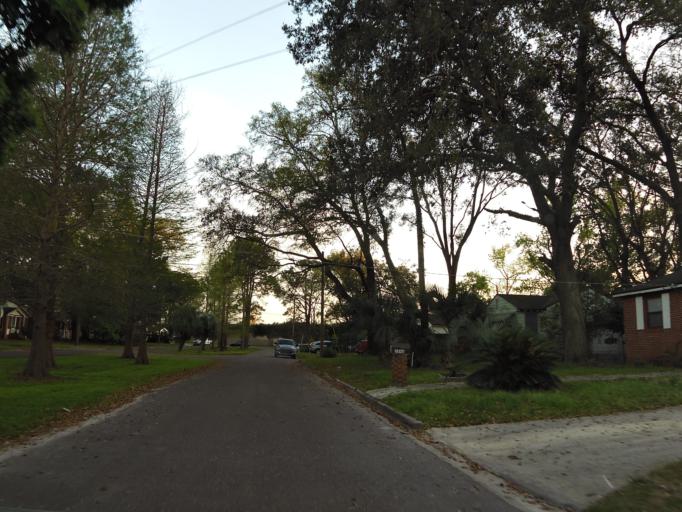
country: US
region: Florida
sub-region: Duval County
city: Jacksonville
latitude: 30.2943
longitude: -81.6320
